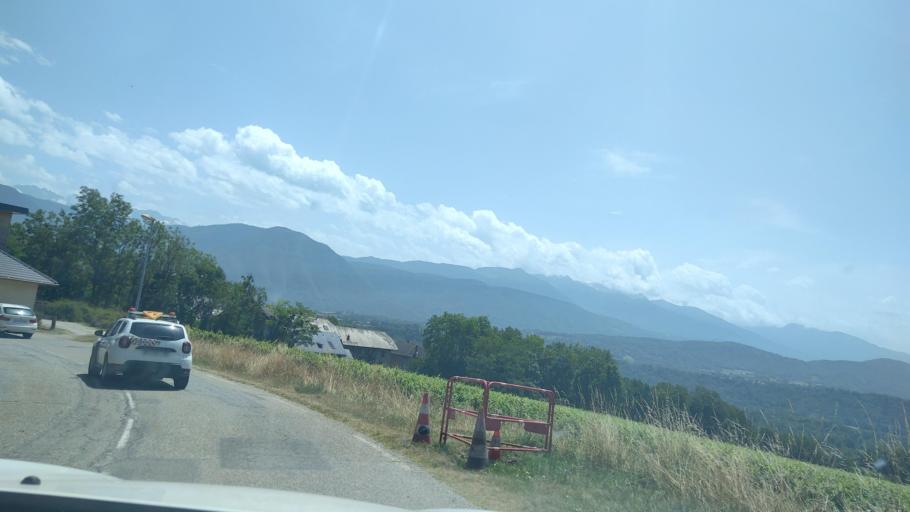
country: FR
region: Rhone-Alpes
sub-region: Departement de la Savoie
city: Coise-Saint-Jean-Pied-Gauthier
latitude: 45.5678
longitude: 6.1513
